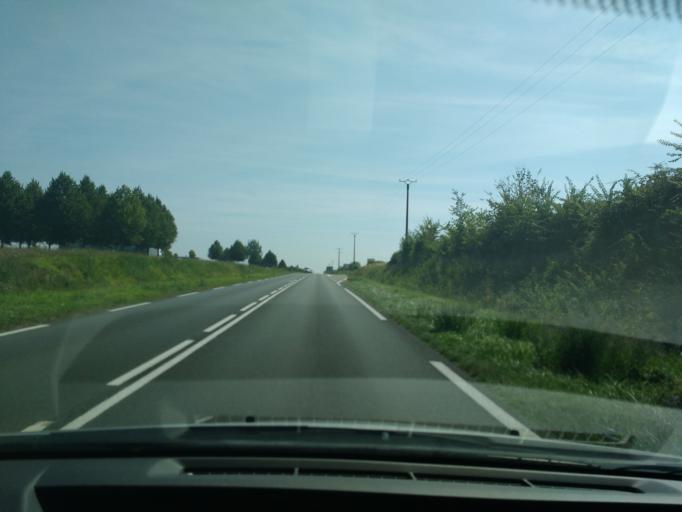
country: FR
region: Pays de la Loire
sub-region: Departement de Maine-et-Loire
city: Corne
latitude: 47.4751
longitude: -0.3496
